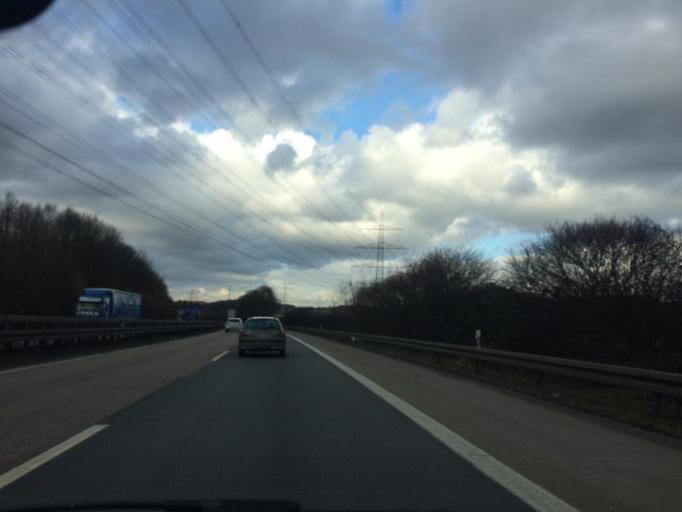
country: DE
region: North Rhine-Westphalia
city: Witten
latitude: 51.4394
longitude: 7.2926
